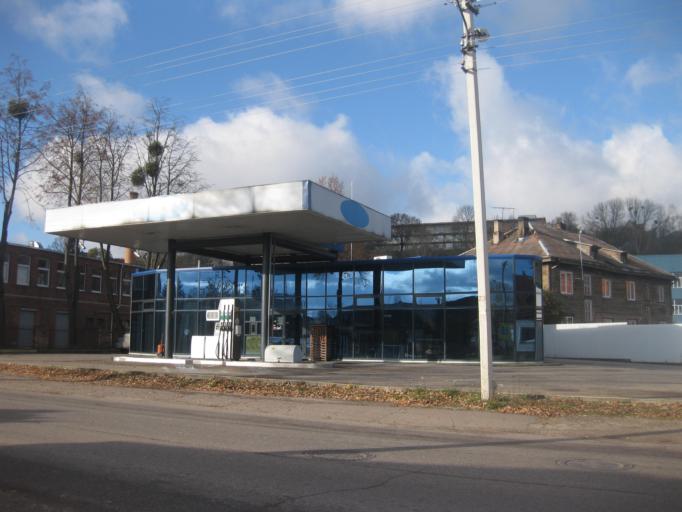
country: LT
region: Kauno apskritis
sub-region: Kaunas
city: Silainiai
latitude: 54.9140
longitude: 23.8874
